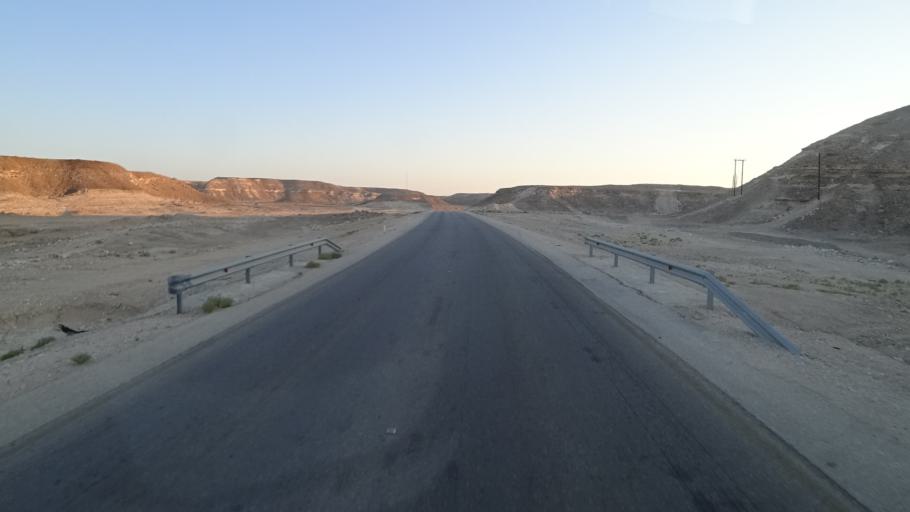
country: OM
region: Zufar
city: Salalah
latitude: 17.4991
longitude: 53.3623
